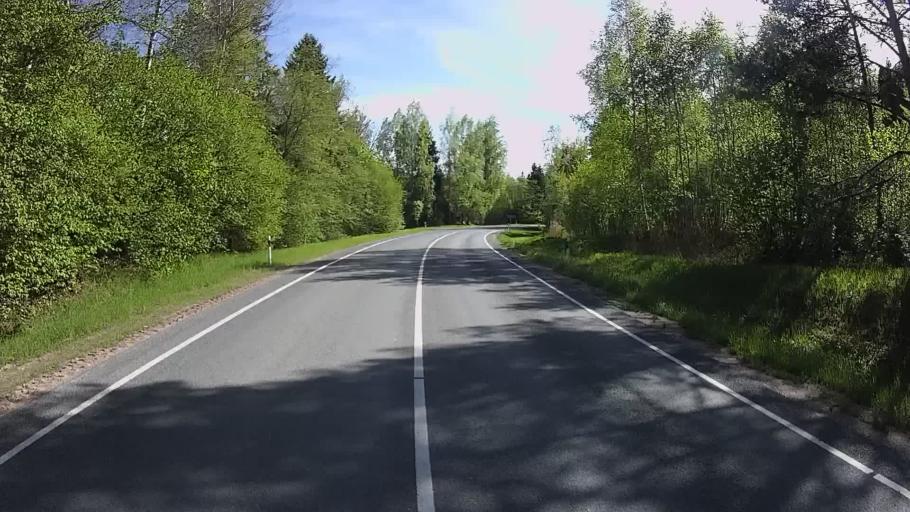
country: EE
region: Vorumaa
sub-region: Antsla vald
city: Vana-Antsla
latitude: 57.9679
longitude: 26.4623
